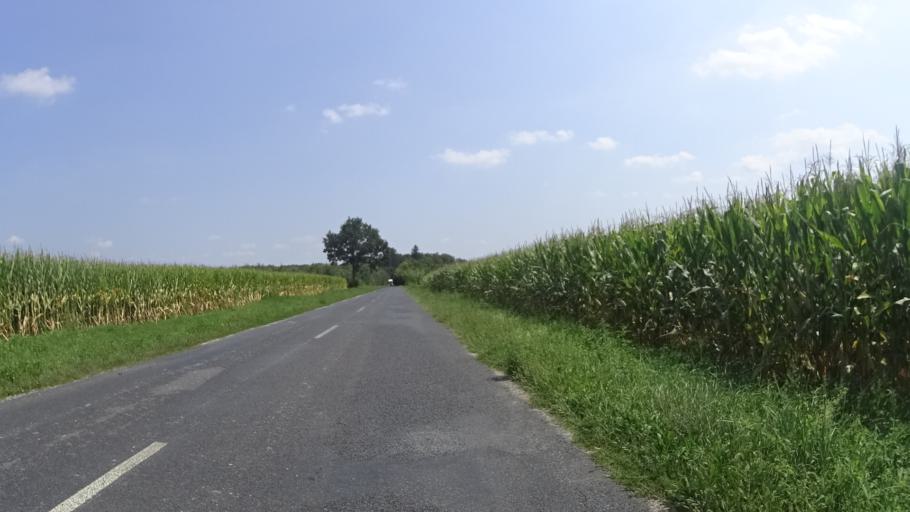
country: HU
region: Zala
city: Murakeresztur
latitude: 46.3716
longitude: 16.8575
